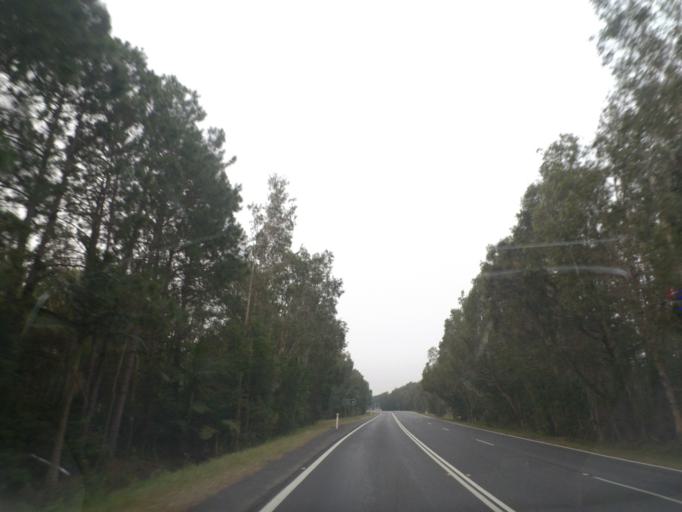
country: AU
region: New South Wales
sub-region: Coffs Harbour
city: Coffs Harbour
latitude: -30.3105
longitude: 153.1179
